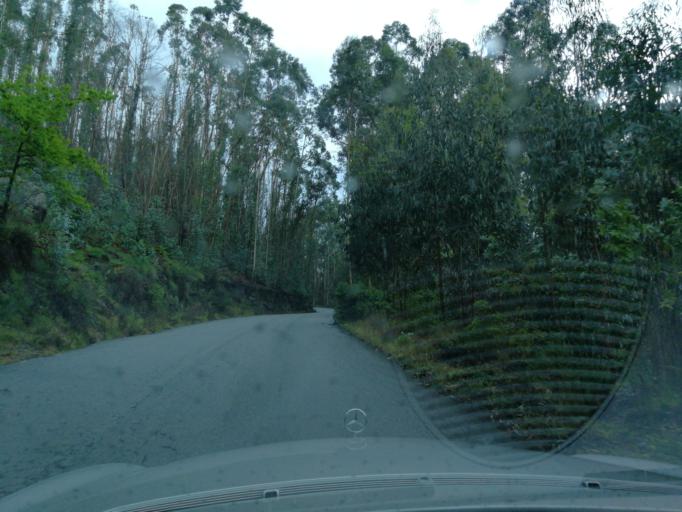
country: PT
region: Braga
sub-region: Braga
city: Oliveira
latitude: 41.4686
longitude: -8.4391
